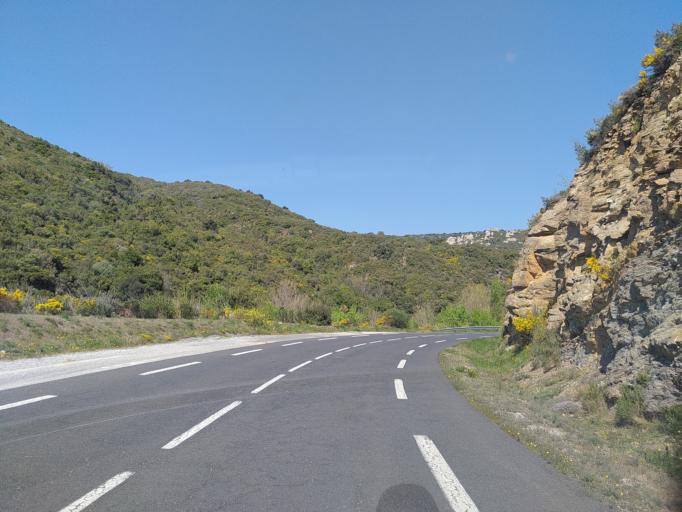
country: FR
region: Languedoc-Roussillon
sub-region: Departement de l'Aude
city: Portel-des-Corbieres
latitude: 42.9870
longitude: 2.7882
